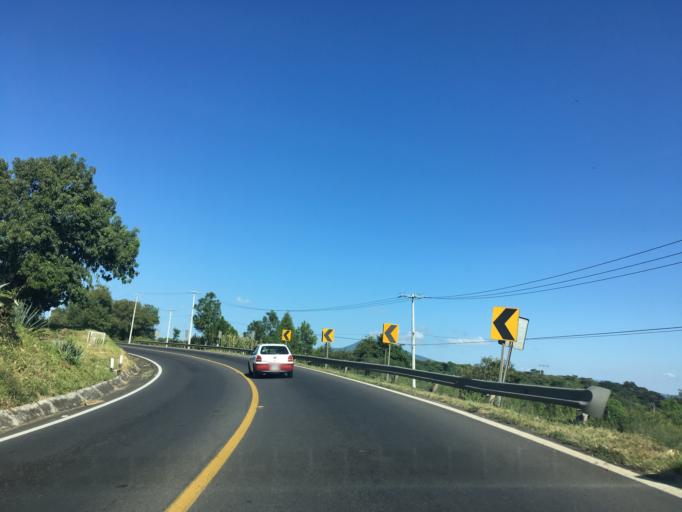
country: MX
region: Mexico
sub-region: Chalco
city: Chilchota
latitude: 19.8555
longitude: -102.1289
